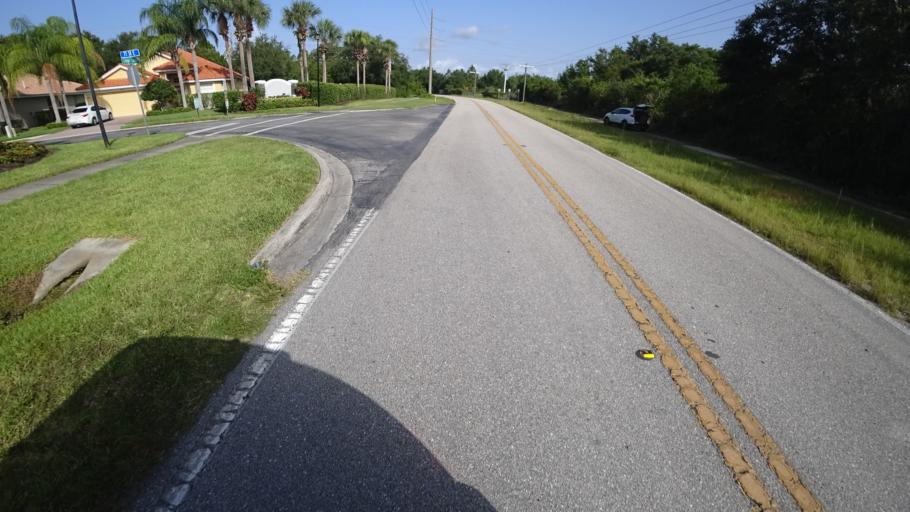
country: US
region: Florida
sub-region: Sarasota County
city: Desoto Lakes
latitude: 27.4212
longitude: -82.4672
